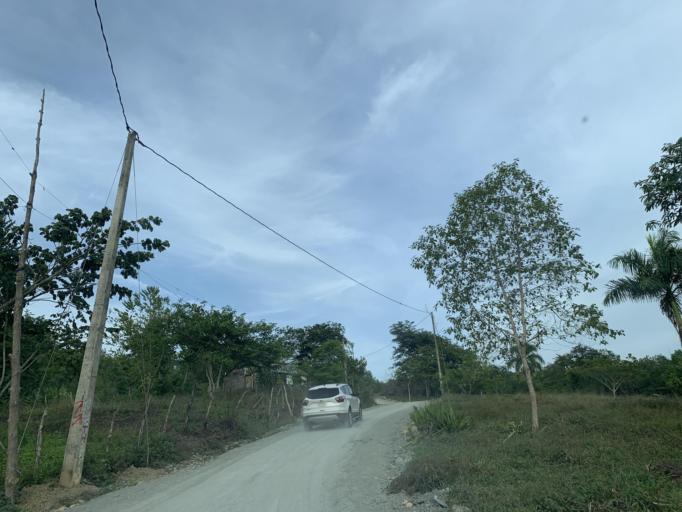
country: DO
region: Santiago
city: Pedro Garcia
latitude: 19.6979
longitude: -70.6209
